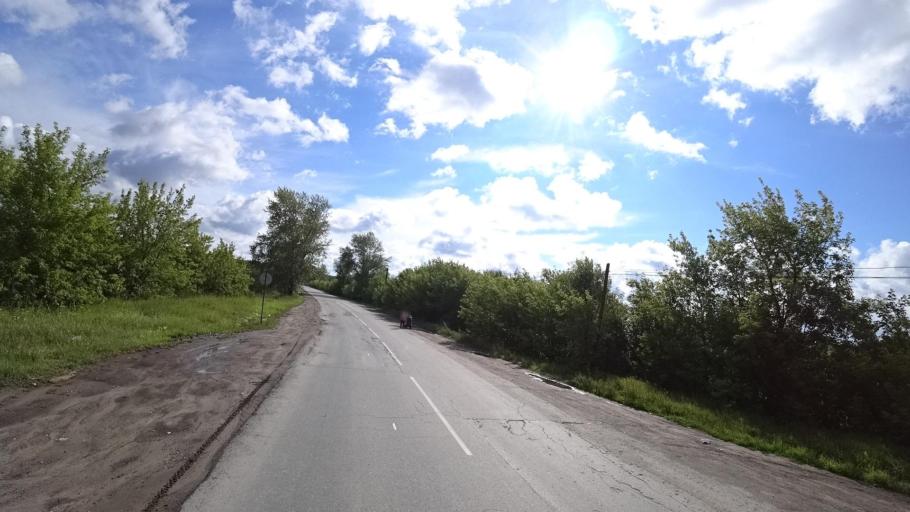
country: RU
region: Sverdlovsk
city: Kamyshlov
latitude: 56.8385
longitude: 62.7009
